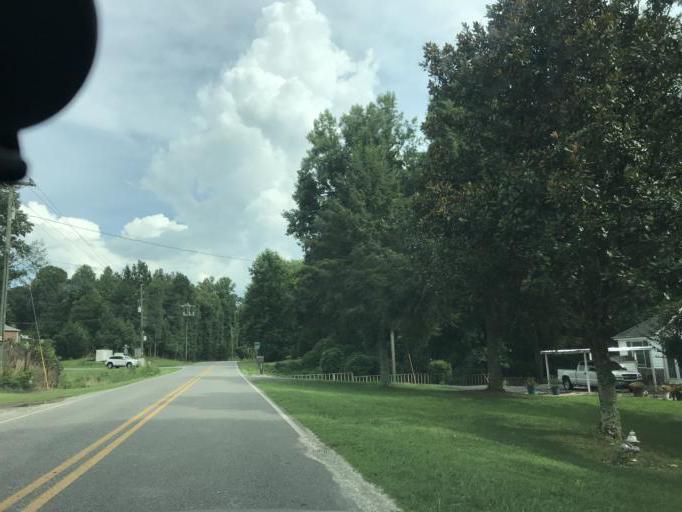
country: US
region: Georgia
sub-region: Forsyth County
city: Cumming
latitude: 34.3102
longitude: -84.1644
